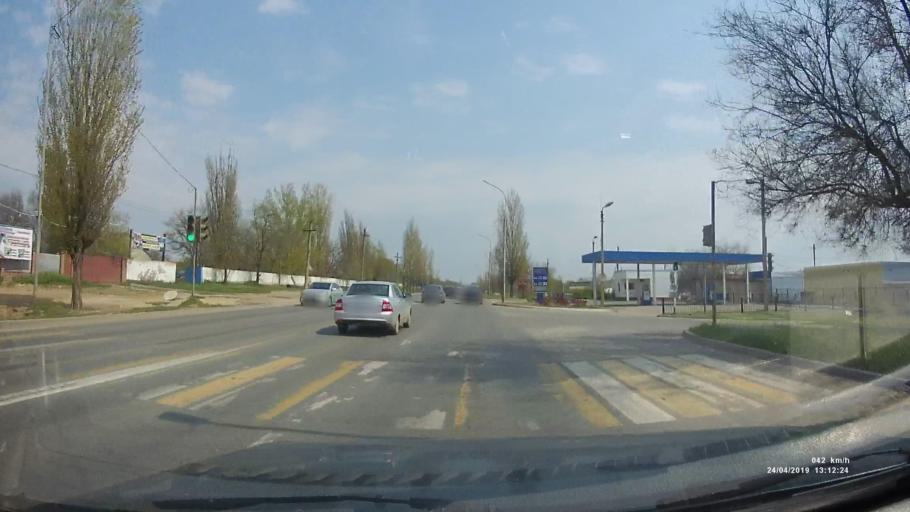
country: RU
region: Kalmykiya
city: Elista
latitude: 46.3128
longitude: 44.3034
